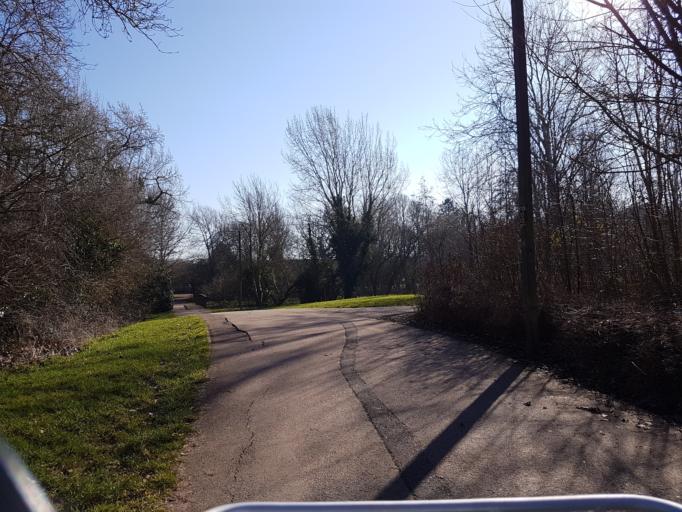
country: GB
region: England
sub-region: Milton Keynes
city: Loughton
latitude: 52.0112
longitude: -0.7621
